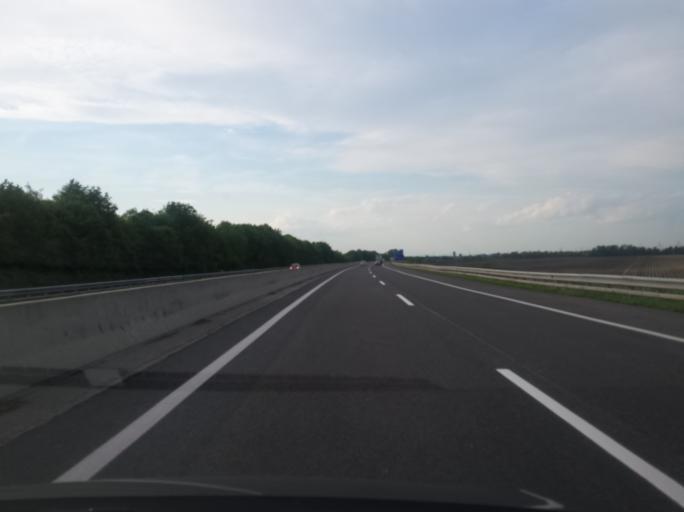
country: AT
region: Lower Austria
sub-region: Politischer Bezirk Baden
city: Ebreichsdorf
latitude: 47.9508
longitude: 16.3684
